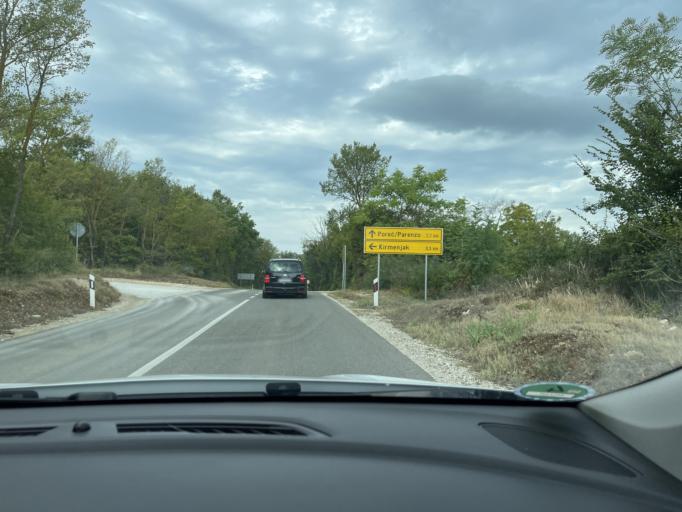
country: HR
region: Istarska
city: Vrsar
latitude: 45.1976
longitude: 13.7076
